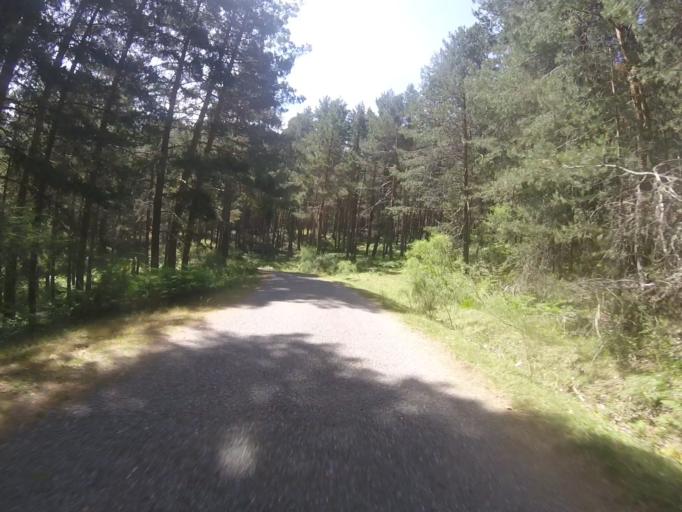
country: ES
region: Madrid
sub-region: Provincia de Madrid
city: Cercedilla
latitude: 40.8069
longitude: -4.0433
